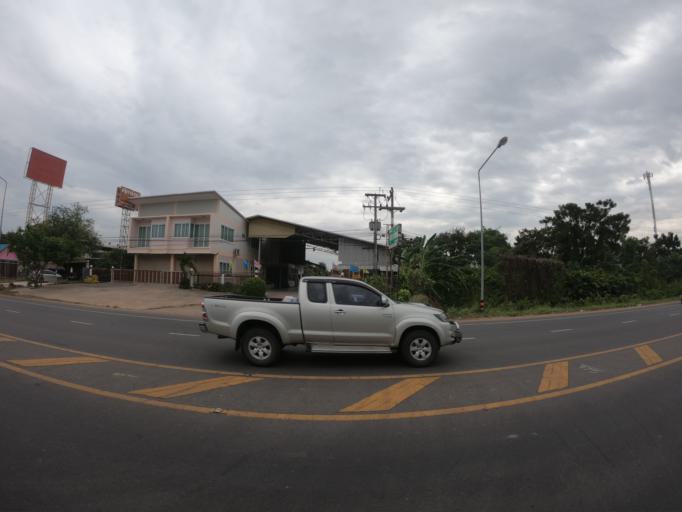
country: TH
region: Roi Et
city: Roi Et
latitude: 16.0801
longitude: 103.6968
